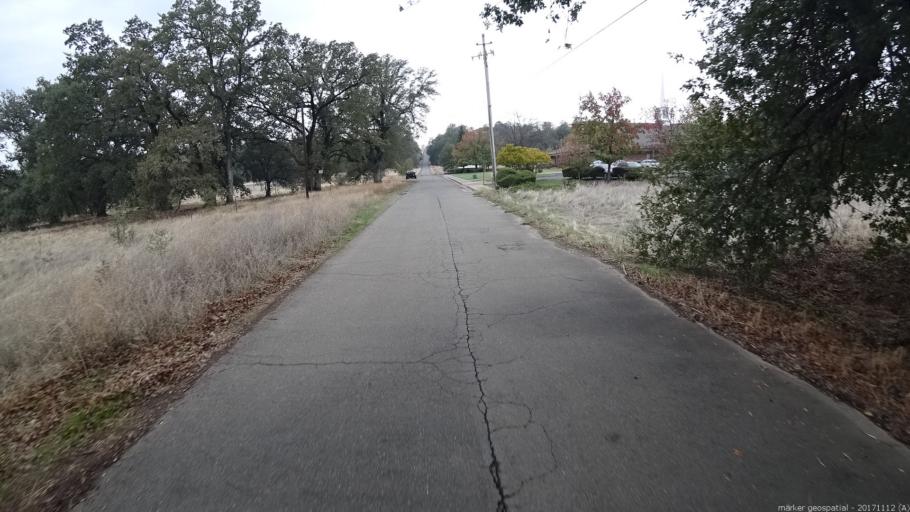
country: US
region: California
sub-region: Shasta County
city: Palo Cedro
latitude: 40.5567
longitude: -122.2414
